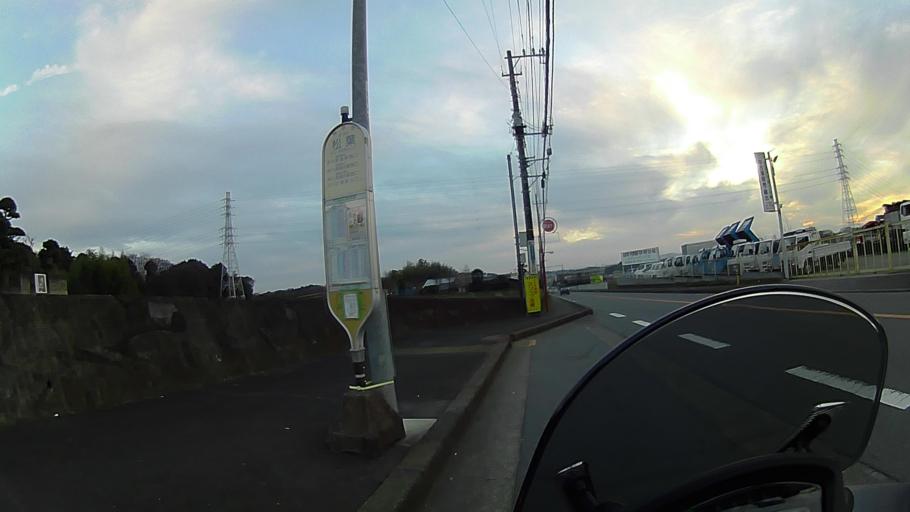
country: JP
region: Kanagawa
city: Atsugi
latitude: 35.4138
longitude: 139.4175
